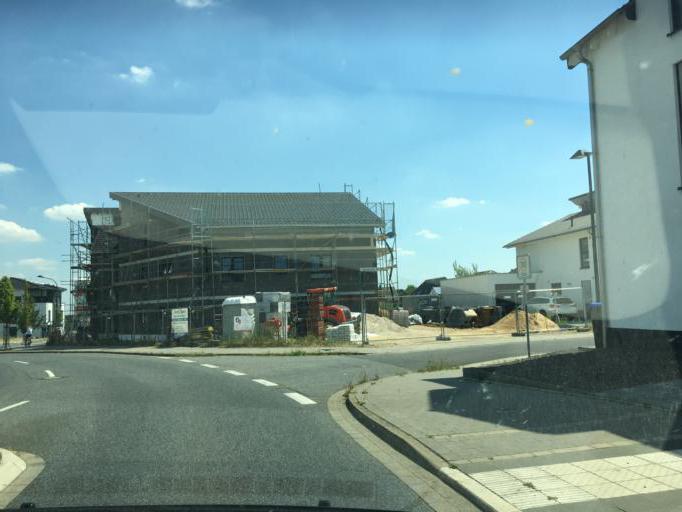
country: DE
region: North Rhine-Westphalia
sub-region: Regierungsbezirk Koln
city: Langerwehe
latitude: 50.8087
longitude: 6.3783
